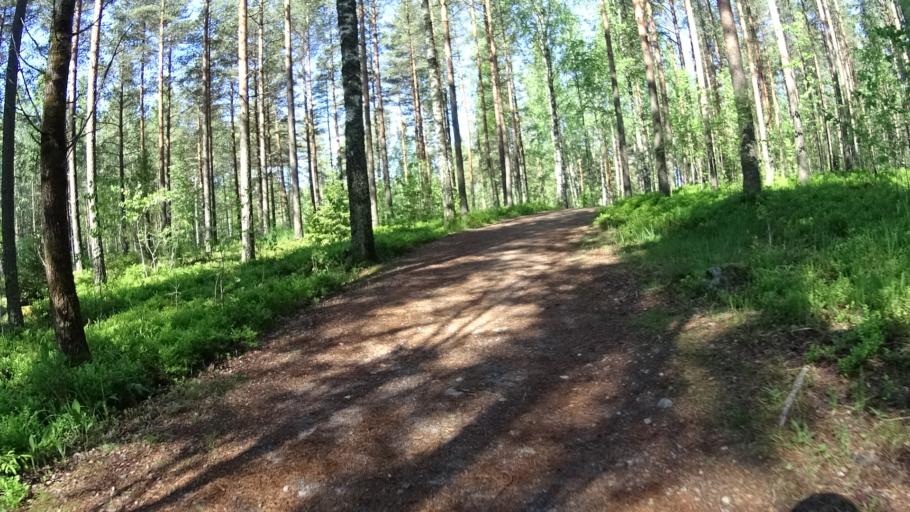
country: FI
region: Uusimaa
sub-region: Helsinki
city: Kauniainen
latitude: 60.3207
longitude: 24.6927
